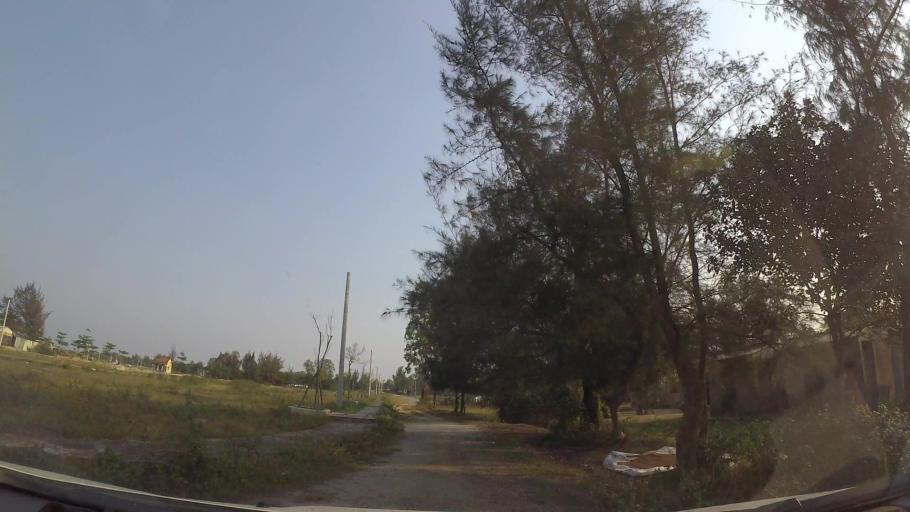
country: VN
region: Da Nang
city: Ngu Hanh Son
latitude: 15.9615
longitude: 108.2651
